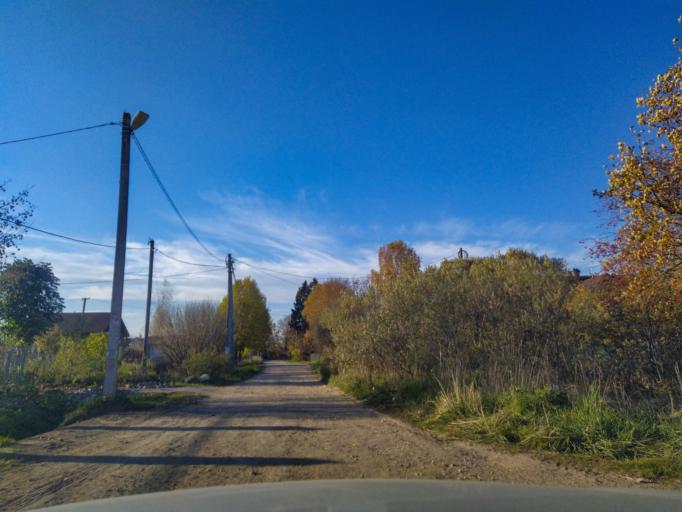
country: RU
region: Leningrad
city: Siverskiy
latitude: 59.3229
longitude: 30.0465
